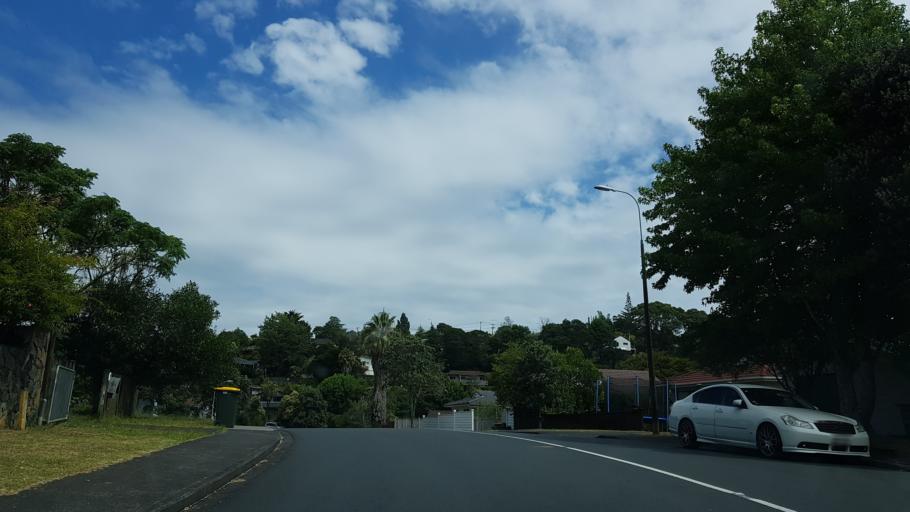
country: NZ
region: Auckland
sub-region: Auckland
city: North Shore
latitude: -36.7716
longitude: 174.7159
